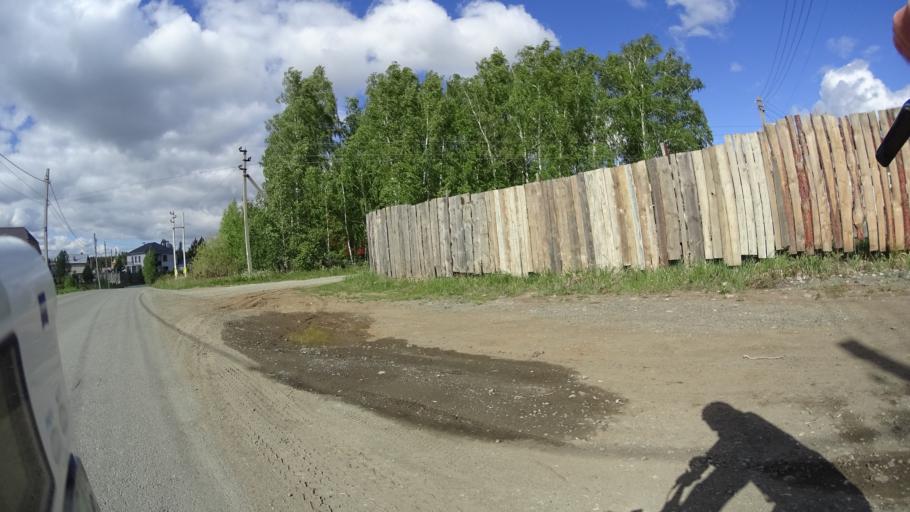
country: RU
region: Chelyabinsk
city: Sargazy
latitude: 55.1604
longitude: 61.2431
